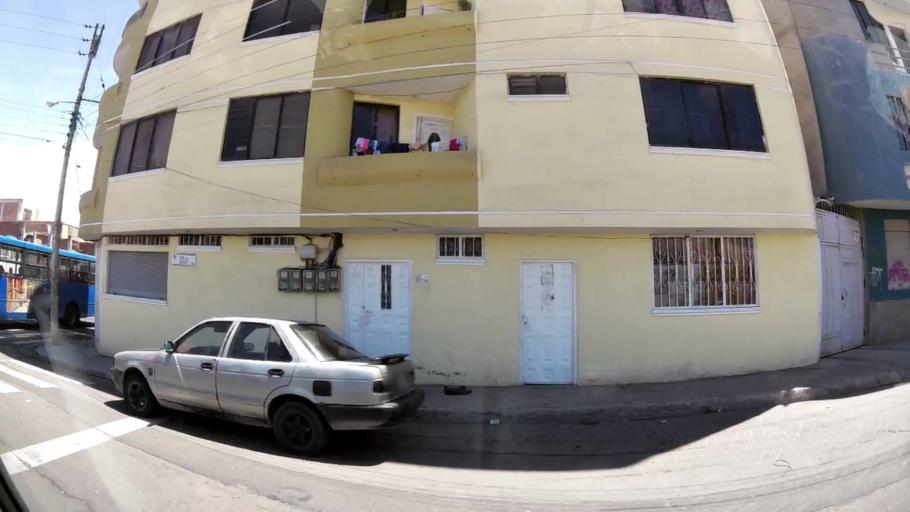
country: EC
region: Chimborazo
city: Riobamba
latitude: -1.6615
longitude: -78.6594
